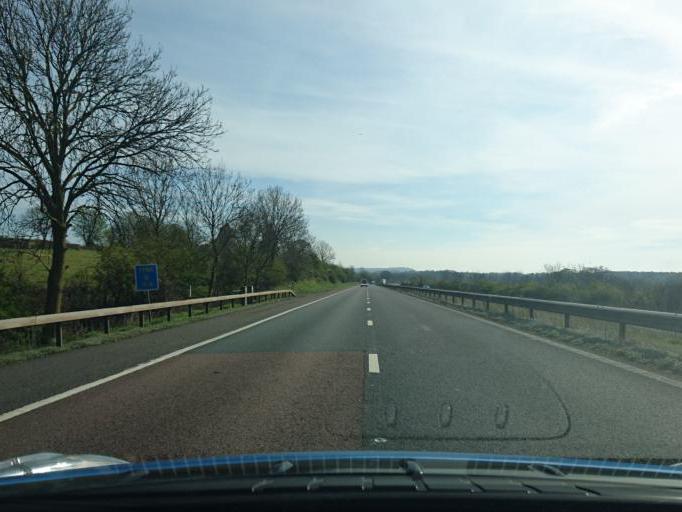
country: GB
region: England
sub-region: Worcestershire
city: Upton upon Severn
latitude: 52.0006
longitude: -2.2715
